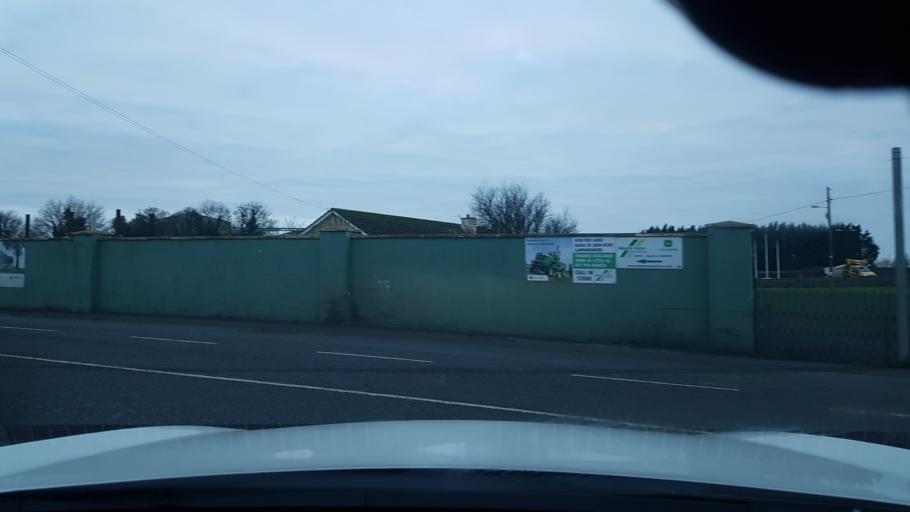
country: IE
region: Leinster
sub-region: An Mhi
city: Navan
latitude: 53.7058
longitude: -6.6849
